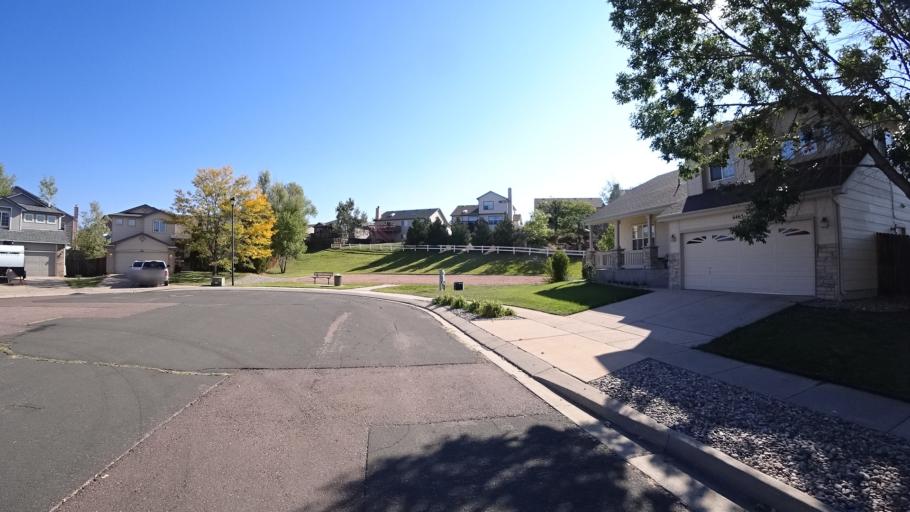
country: US
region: Colorado
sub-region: El Paso County
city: Cimarron Hills
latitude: 38.8828
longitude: -104.7062
